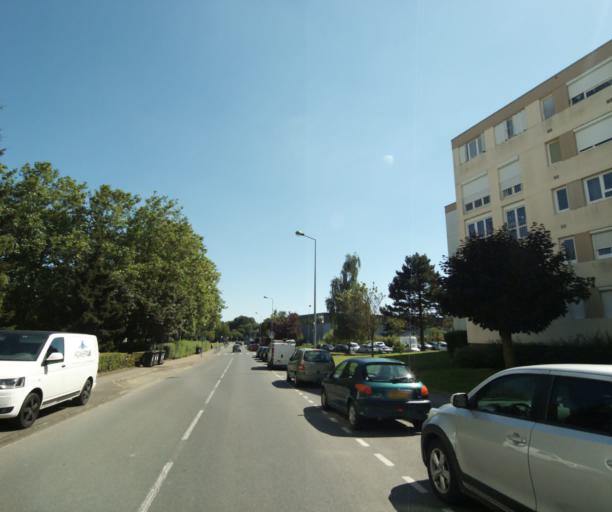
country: FR
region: Pays de la Loire
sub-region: Departement de la Mayenne
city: Laval
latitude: 48.0634
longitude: -0.7522
